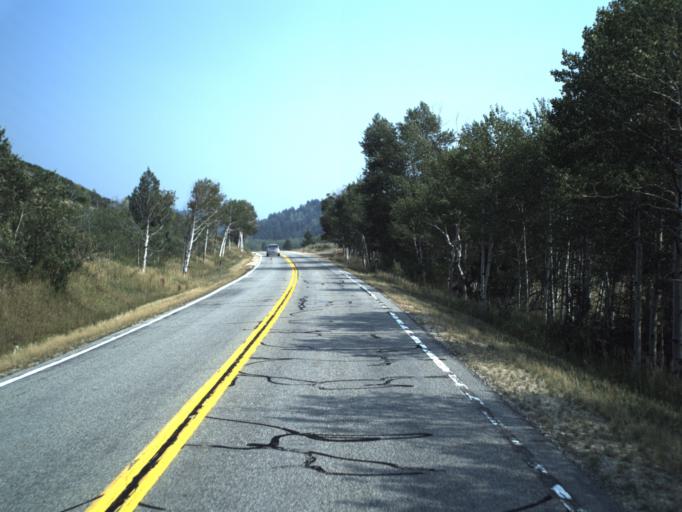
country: US
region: Utah
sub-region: Summit County
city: Francis
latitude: 40.6244
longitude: -111.1577
